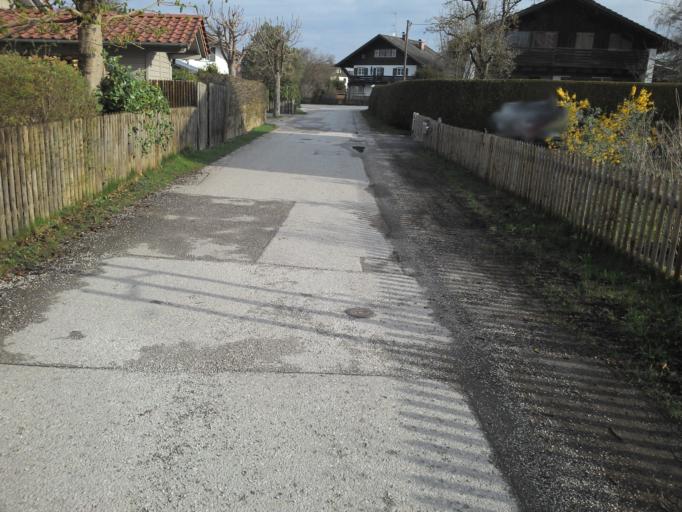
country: DE
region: Bavaria
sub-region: Upper Bavaria
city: Seeshaupt
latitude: 47.8216
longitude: 11.3060
